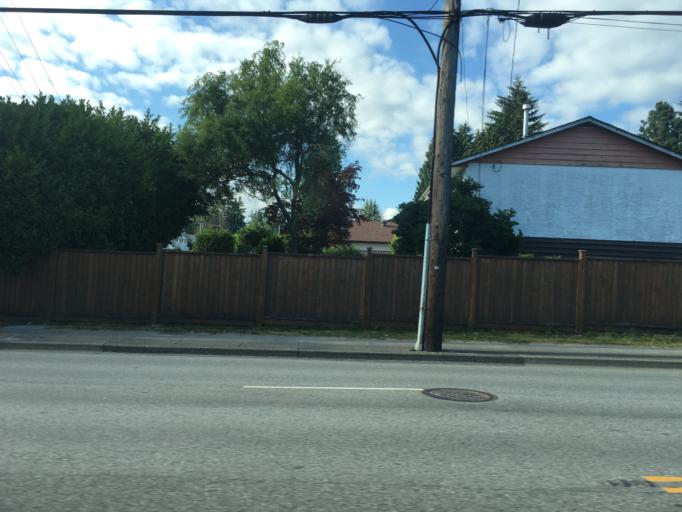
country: CA
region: British Columbia
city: Port Moody
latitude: 49.2490
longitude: -122.8368
